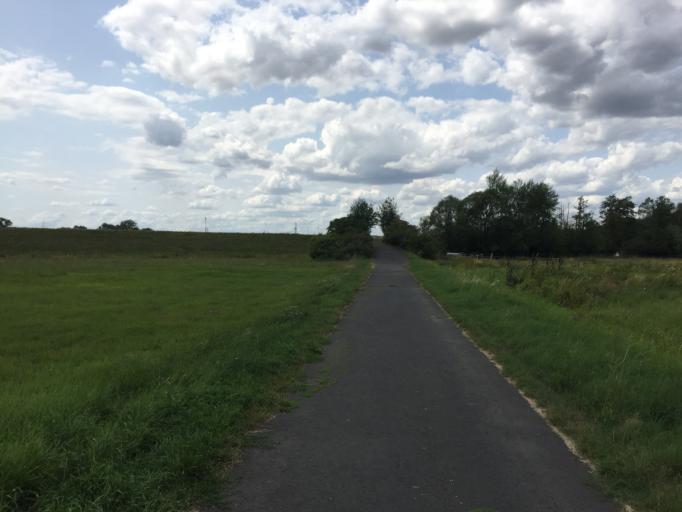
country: DE
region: Hesse
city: Schwalmstadt
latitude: 50.9165
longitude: 9.2322
